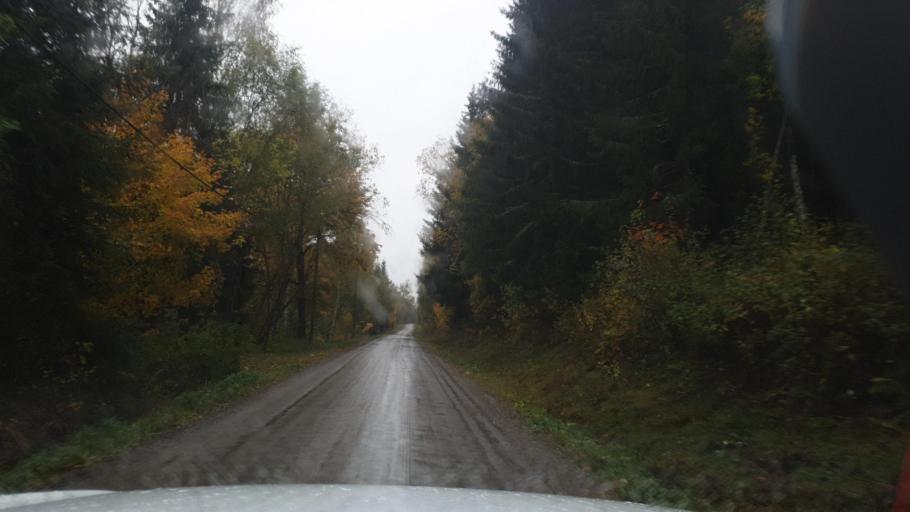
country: SE
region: Vaermland
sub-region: Eda Kommun
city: Amotfors
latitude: 59.7449
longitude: 12.2757
